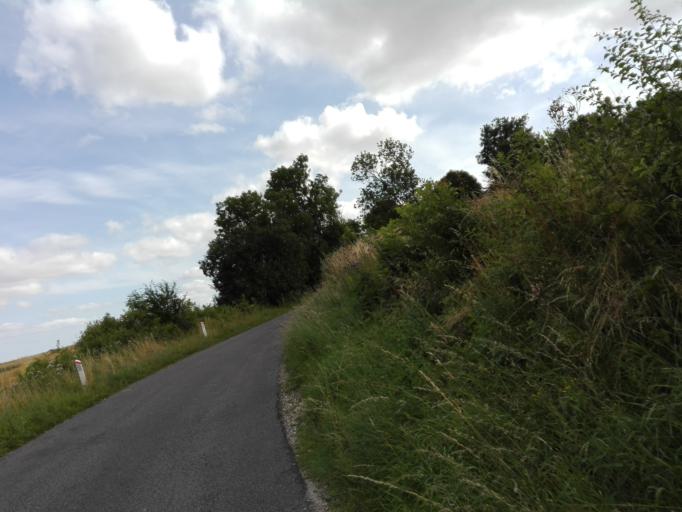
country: DK
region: Central Jutland
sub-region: Skanderborg Kommune
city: Horning
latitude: 56.0994
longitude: 10.0212
